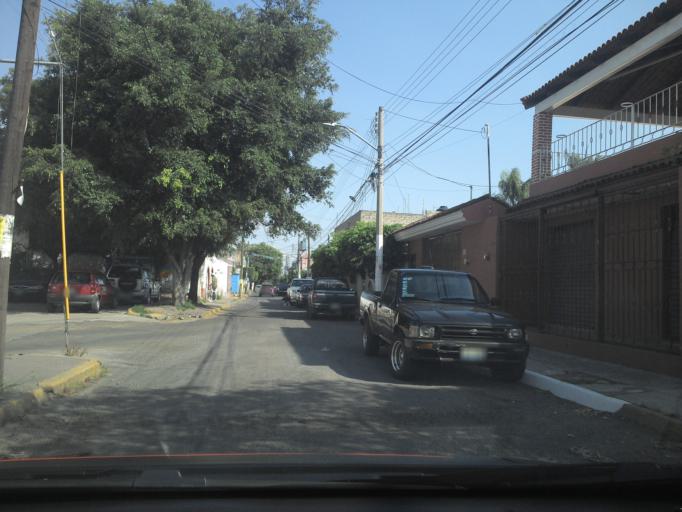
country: MX
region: Jalisco
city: Guadalajara
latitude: 20.6480
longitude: -103.4402
